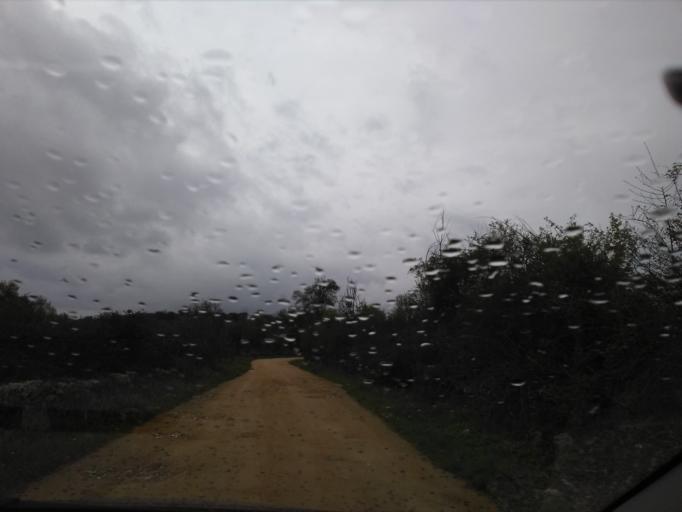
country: ES
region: Castille and Leon
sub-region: Provincia de Salamanca
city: San Felices de los Gallegos
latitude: 40.8433
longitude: -6.7242
